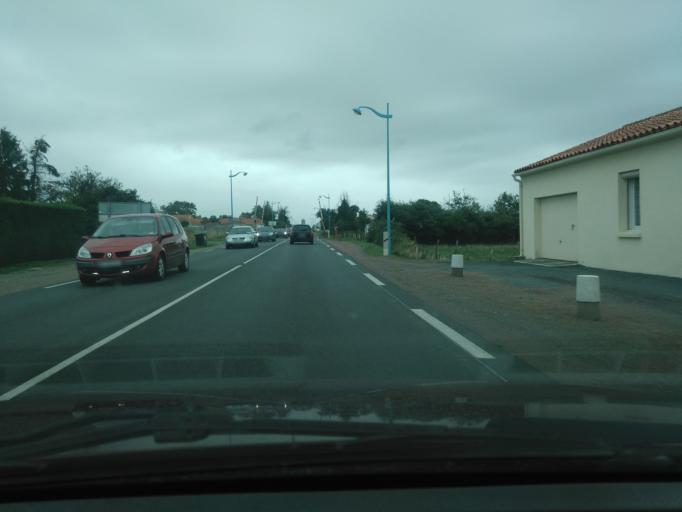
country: FR
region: Pays de la Loire
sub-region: Departement de la Vendee
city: Sainte-Gemme-la-Plaine
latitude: 46.4703
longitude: -1.1096
